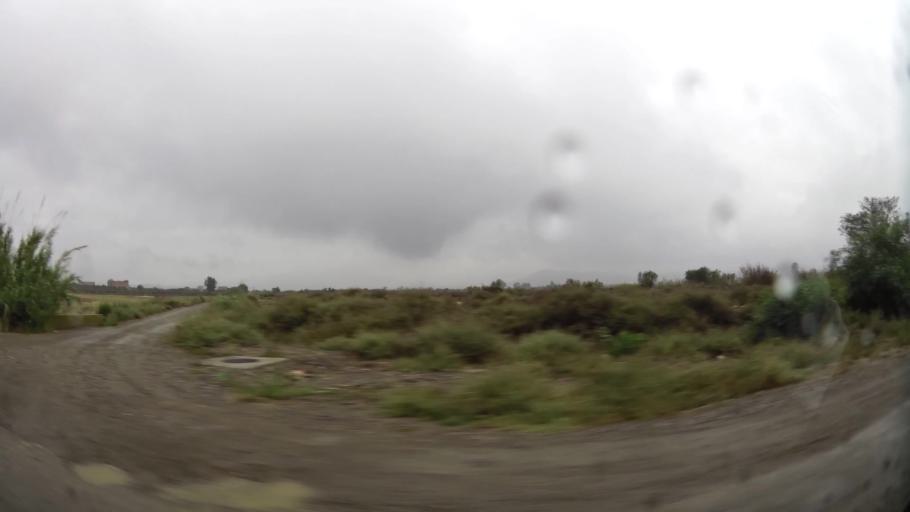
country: MA
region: Taza-Al Hoceima-Taounate
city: Imzourene
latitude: 35.1449
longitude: -3.8118
